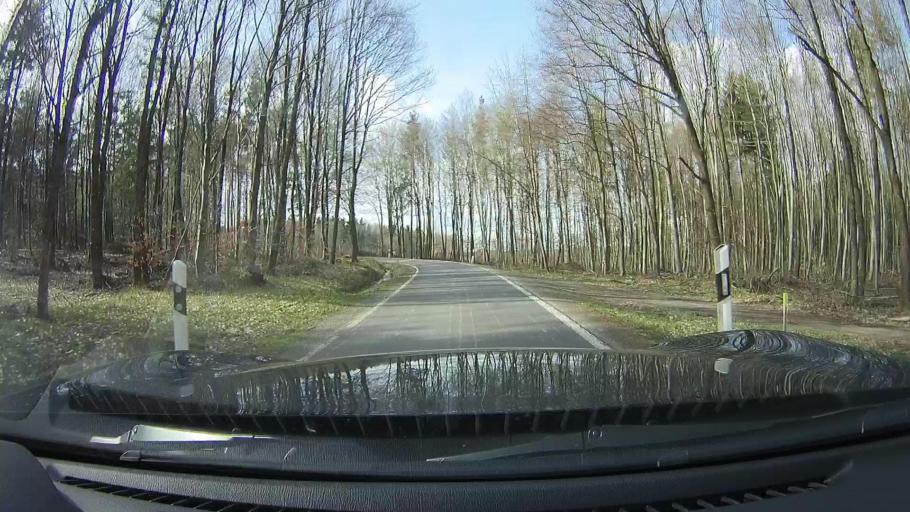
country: DE
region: Bavaria
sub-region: Regierungsbezirk Unterfranken
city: Weilbach
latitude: 49.6151
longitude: 9.2792
